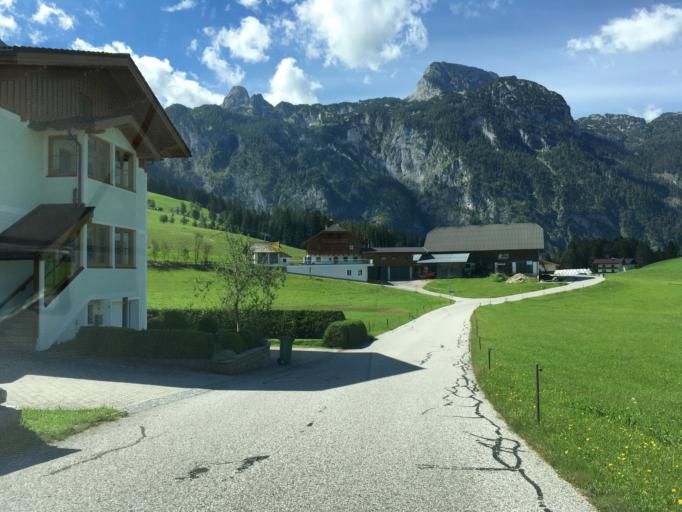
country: AT
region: Salzburg
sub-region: Politischer Bezirk Hallein
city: Abtenau
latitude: 47.5587
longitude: 13.3536
